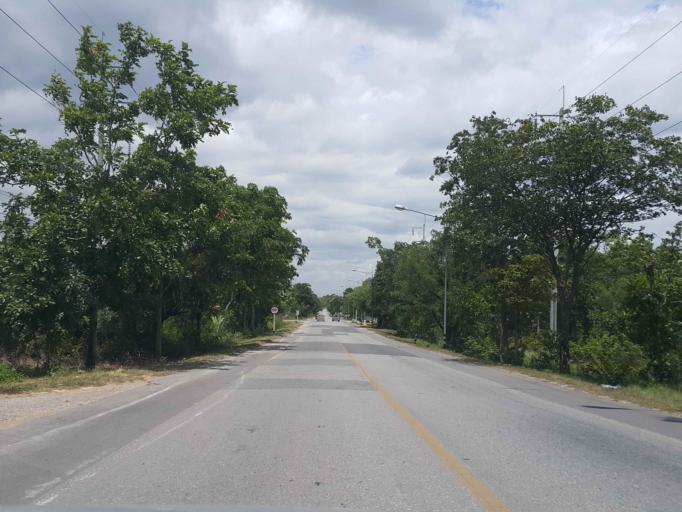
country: TH
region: Lamphun
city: Ban Hong
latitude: 18.3725
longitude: 98.8141
